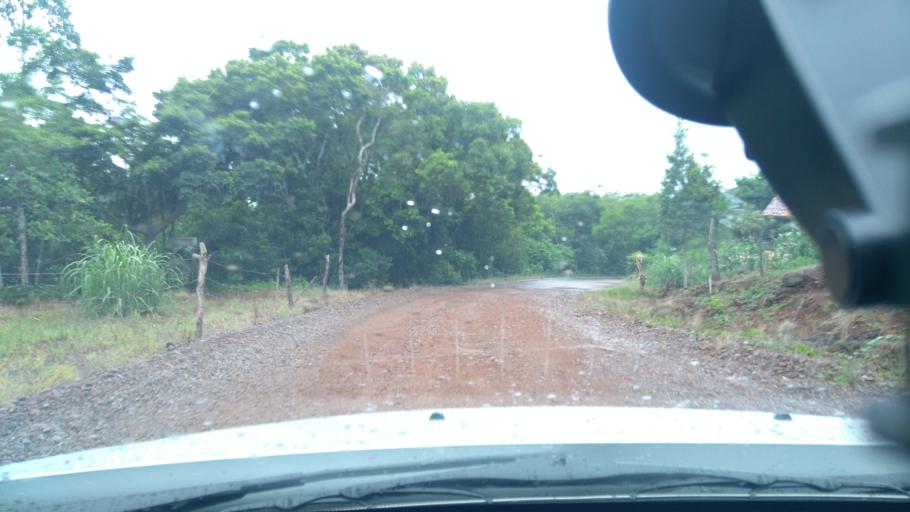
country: BR
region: Rio Grande do Sul
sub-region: Torres
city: Torres
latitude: -29.1807
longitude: -49.9862
